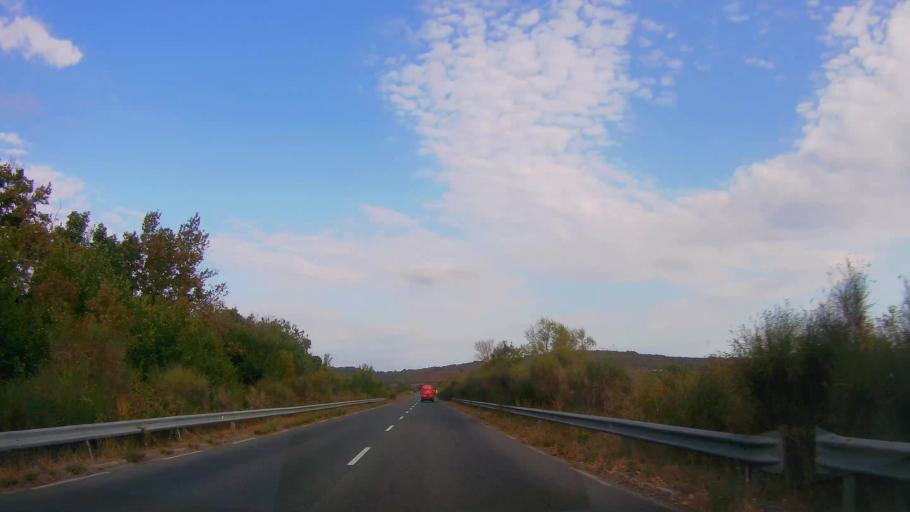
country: BG
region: Burgas
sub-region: Obshtina Sozopol
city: Sozopol
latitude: 42.3587
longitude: 27.7028
